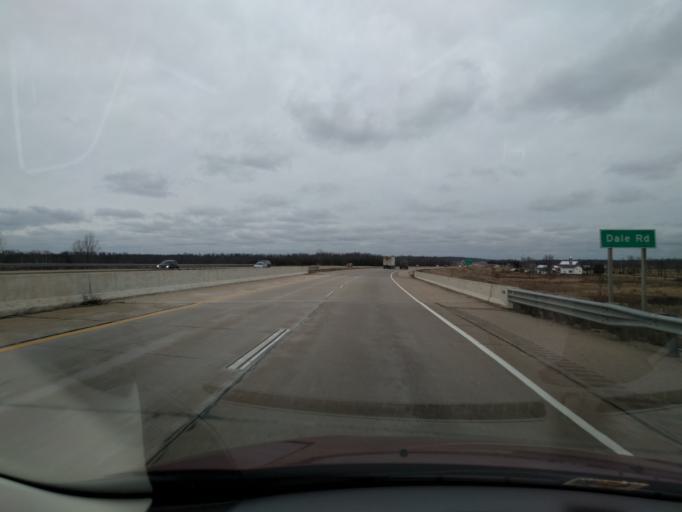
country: US
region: Wisconsin
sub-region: Winnebago County
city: Winneconne
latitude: 44.2241
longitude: -88.7057
